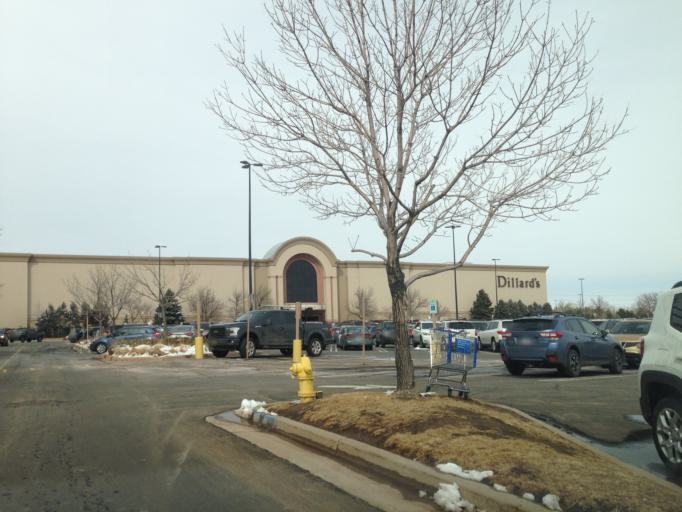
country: US
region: Colorado
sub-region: Boulder County
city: Superior
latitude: 39.9310
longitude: -105.1316
